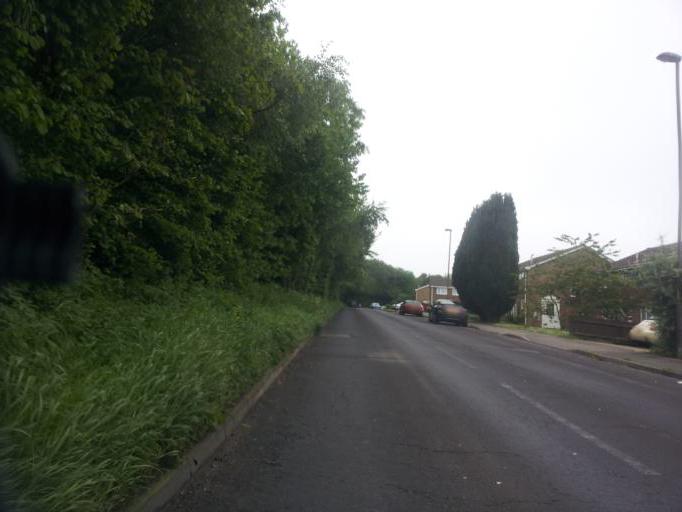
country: GB
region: England
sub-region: Kent
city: Boxley
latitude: 51.3278
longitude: 0.5513
